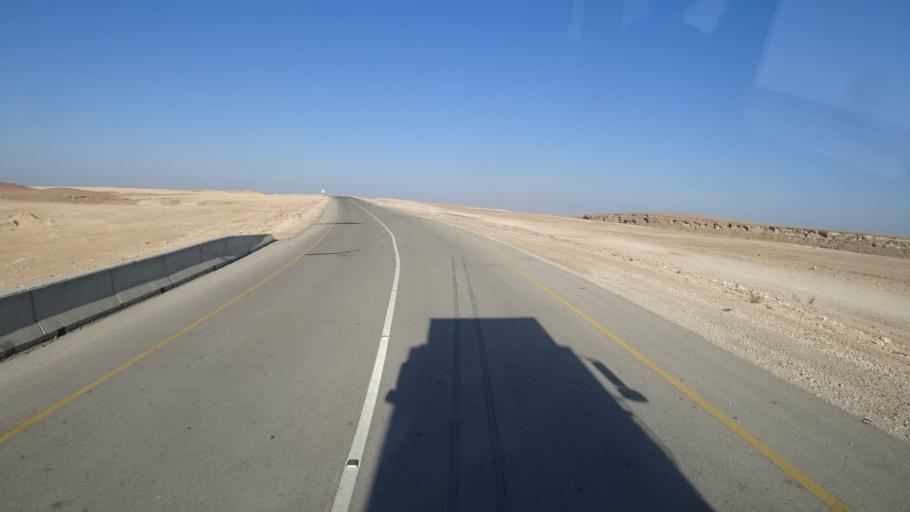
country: YE
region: Al Mahrah
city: Hawf
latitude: 17.0750
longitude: 53.0281
